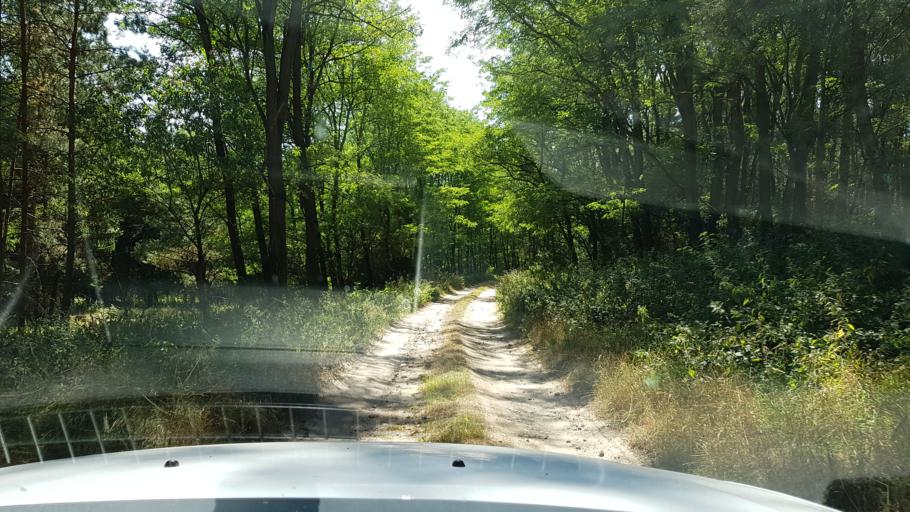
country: PL
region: West Pomeranian Voivodeship
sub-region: Powiat gryfinski
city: Cedynia
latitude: 52.8395
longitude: 14.2554
